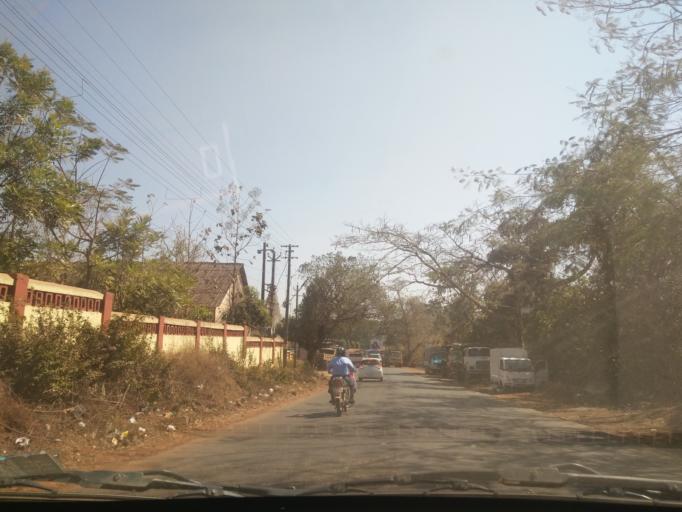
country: IN
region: Goa
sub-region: North Goa
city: Sanquelim
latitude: 15.5704
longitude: 74.0000
